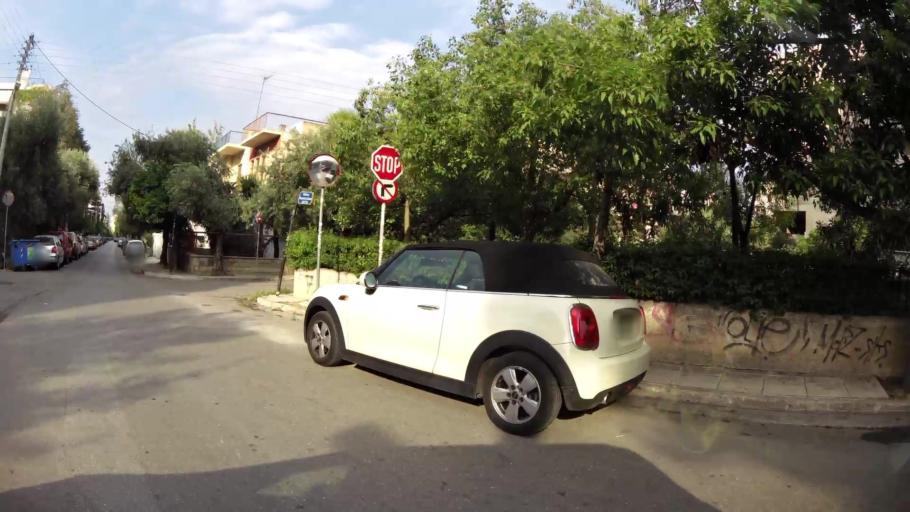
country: GR
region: Attica
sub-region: Nomarchia Athinas
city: Palaio Faliro
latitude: 37.9322
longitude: 23.7086
